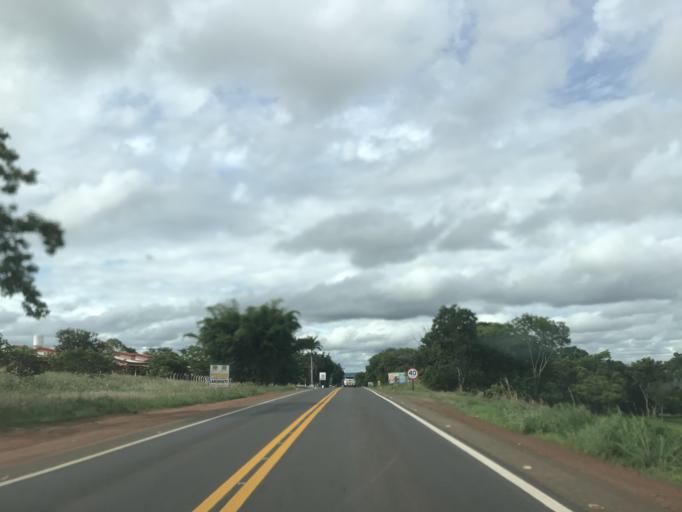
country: BR
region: Goias
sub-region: Piracanjuba
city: Piracanjuba
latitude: -17.2179
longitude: -48.7105
